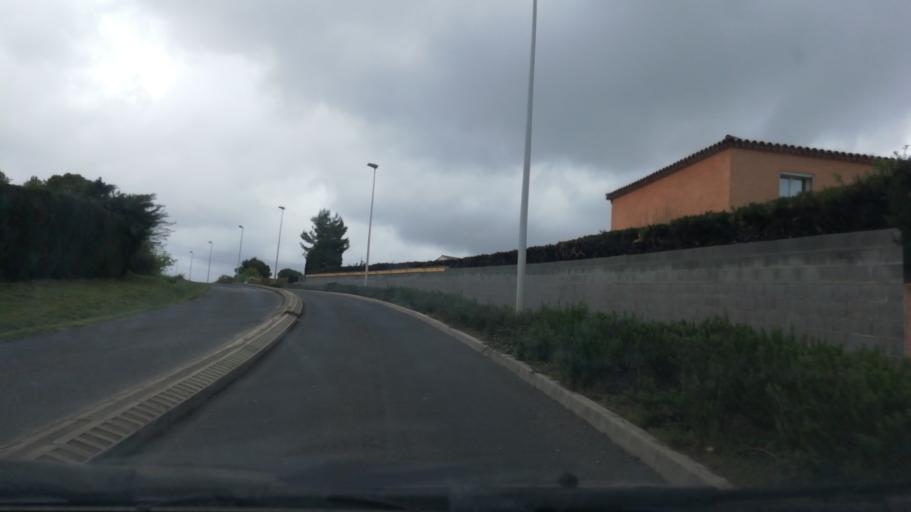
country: FR
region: Languedoc-Roussillon
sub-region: Departement de l'Herault
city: Saint-Gely-du-Fesc
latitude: 43.7018
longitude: 3.8036
